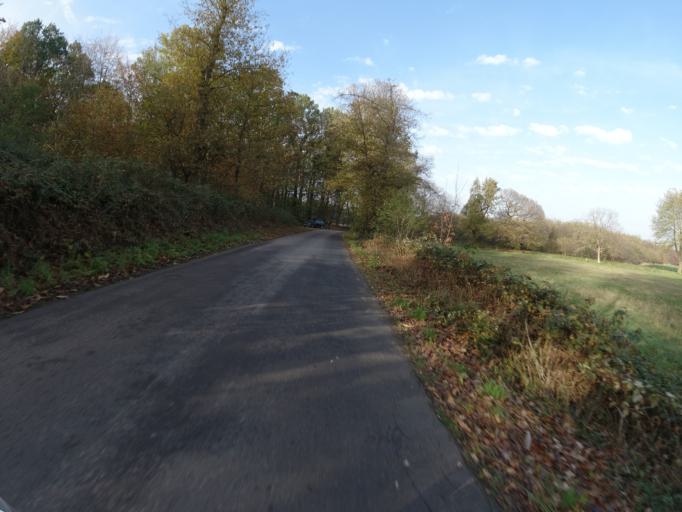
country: DE
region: North Rhine-Westphalia
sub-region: Regierungsbezirk Dusseldorf
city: Moers
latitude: 51.4050
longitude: 6.6288
